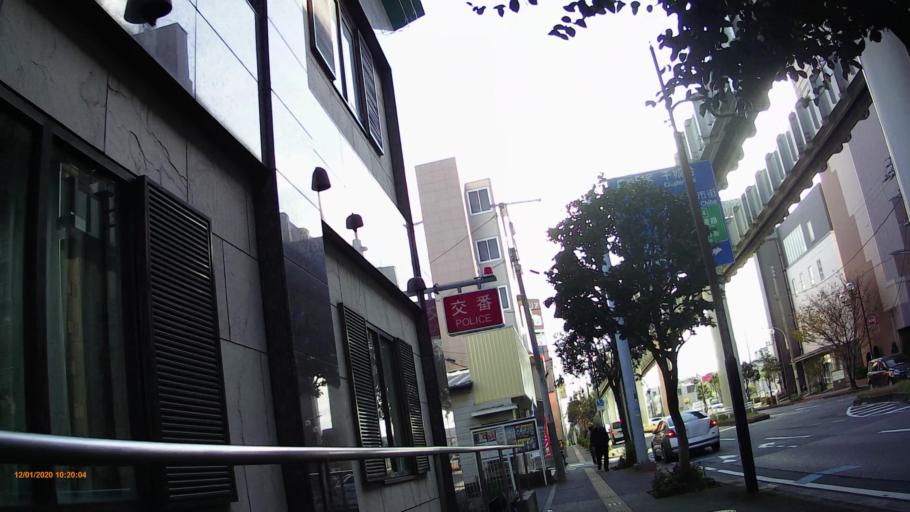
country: JP
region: Chiba
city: Yotsukaido
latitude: 35.6356
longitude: 140.1509
